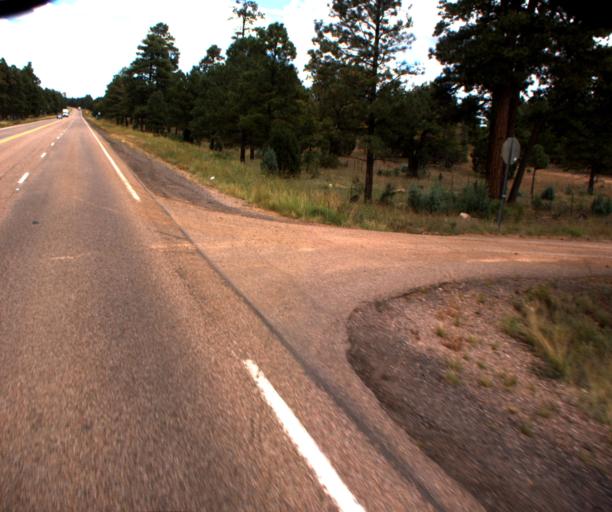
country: US
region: Arizona
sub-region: Navajo County
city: Heber-Overgaard
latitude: 34.4054
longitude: -110.6665
